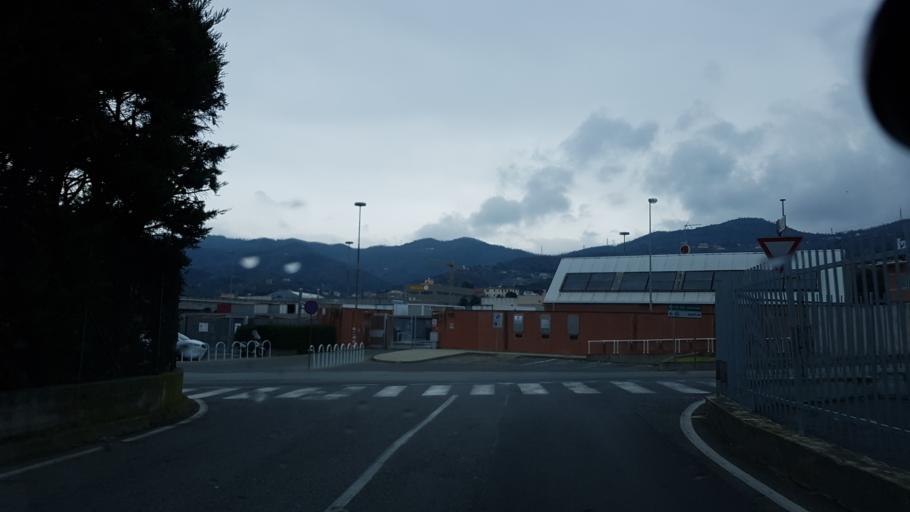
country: IT
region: Liguria
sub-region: Provincia di Savona
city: Savona
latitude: 44.2994
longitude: 8.4567
